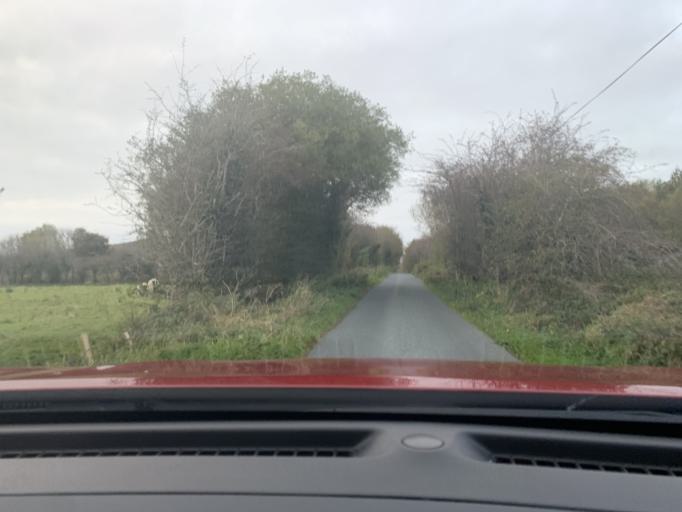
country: IE
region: Connaught
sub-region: Sligo
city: Tobercurry
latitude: 54.0705
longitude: -8.6797
